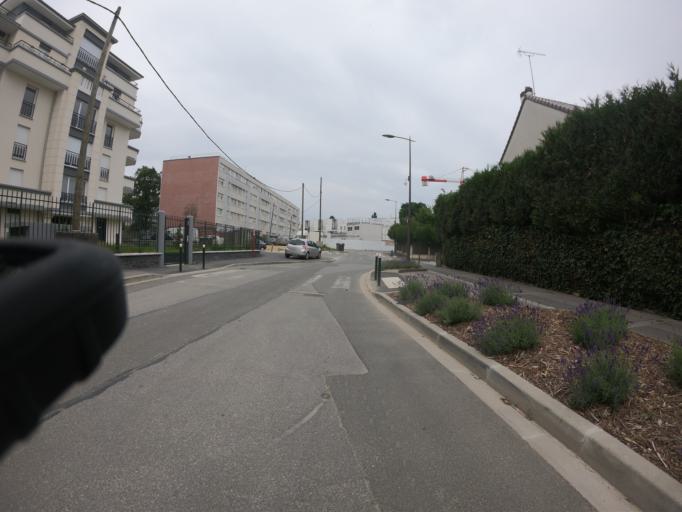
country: FR
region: Ile-de-France
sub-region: Departement du Val-de-Marne
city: Thiais
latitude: 48.7652
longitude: 2.3832
